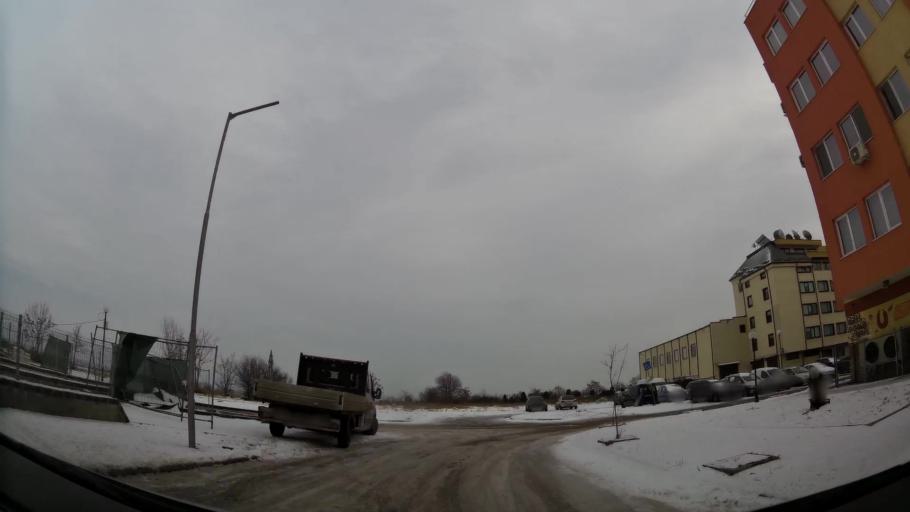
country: BG
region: Sofia-Capital
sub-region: Stolichna Obshtina
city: Sofia
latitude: 42.7159
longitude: 23.3791
